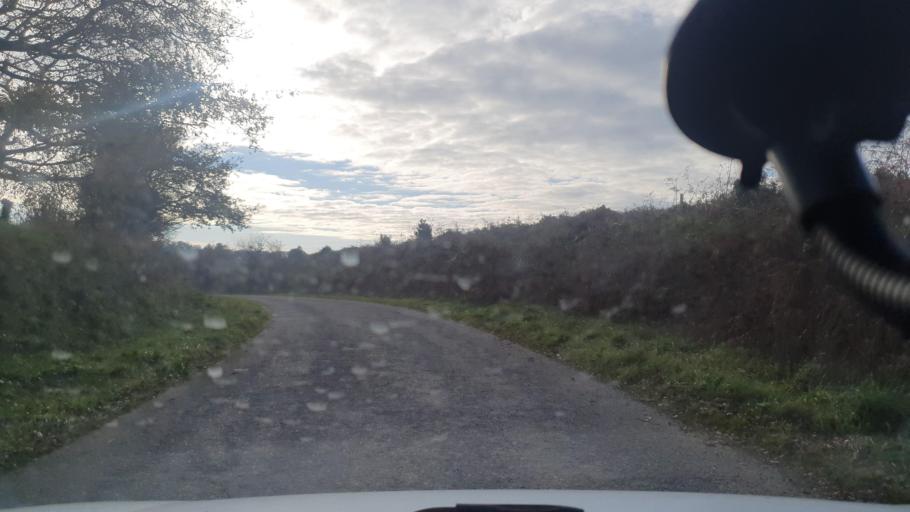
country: FR
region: Brittany
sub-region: Departement du Finistere
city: Landrevarzec
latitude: 48.1019
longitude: -4.0333
